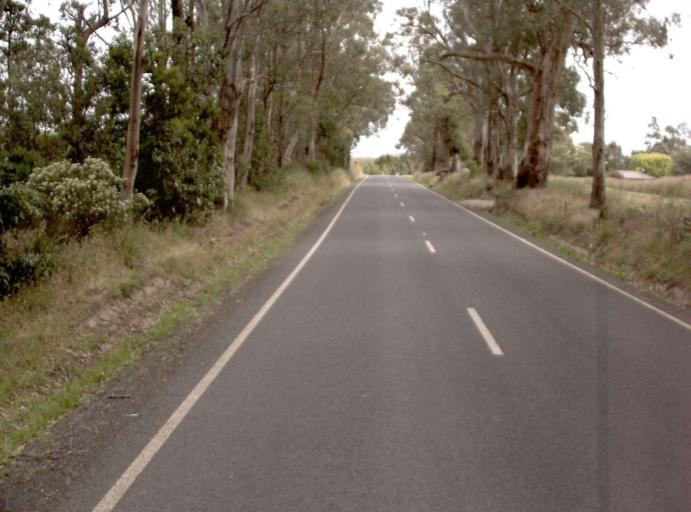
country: AU
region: Victoria
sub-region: Latrobe
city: Moe
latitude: -38.0355
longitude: 146.1660
